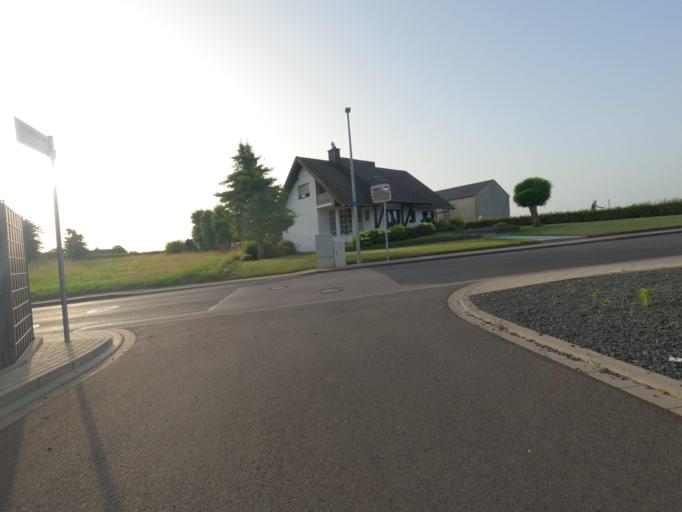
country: DE
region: North Rhine-Westphalia
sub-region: Regierungsbezirk Koln
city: Wassenberg
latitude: 51.0924
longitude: 6.1891
